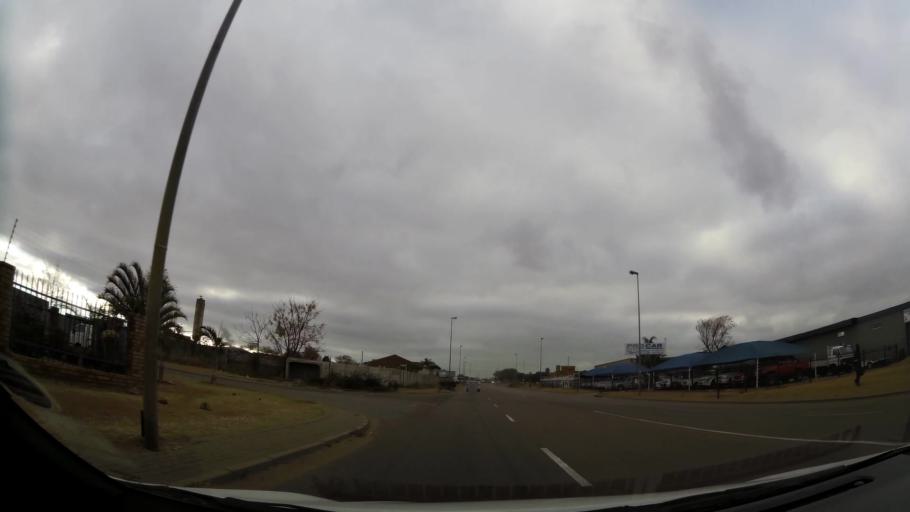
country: ZA
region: Limpopo
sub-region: Capricorn District Municipality
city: Polokwane
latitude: -23.8771
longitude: 29.4376
